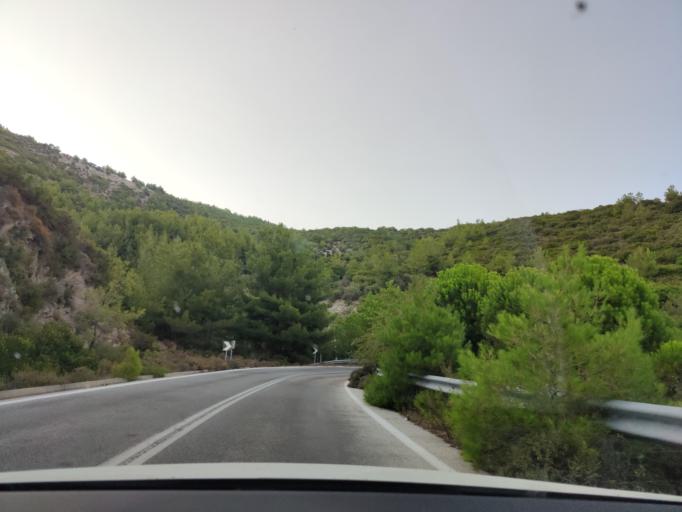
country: GR
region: East Macedonia and Thrace
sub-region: Nomos Kavalas
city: Potamia
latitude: 40.6212
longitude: 24.7589
